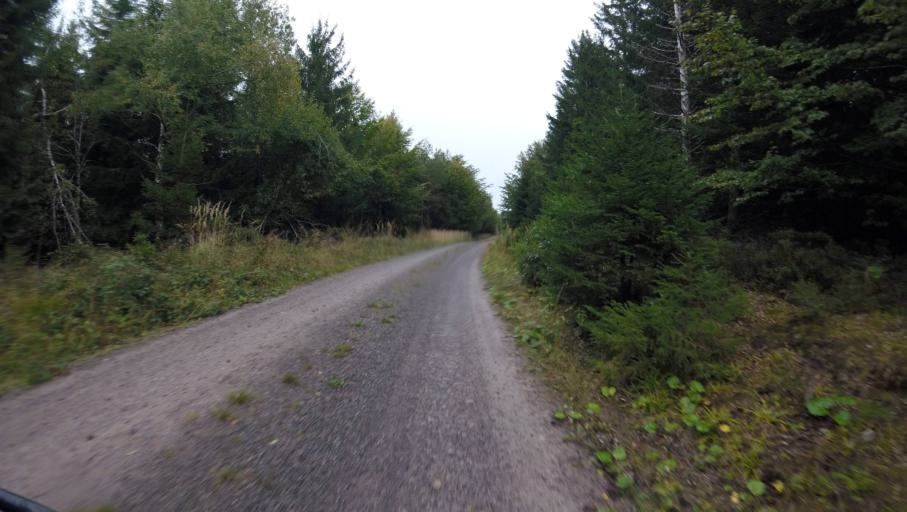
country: DE
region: Baden-Wuerttemberg
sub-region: Karlsruhe Region
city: Forbach
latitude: 48.6595
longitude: 8.4094
